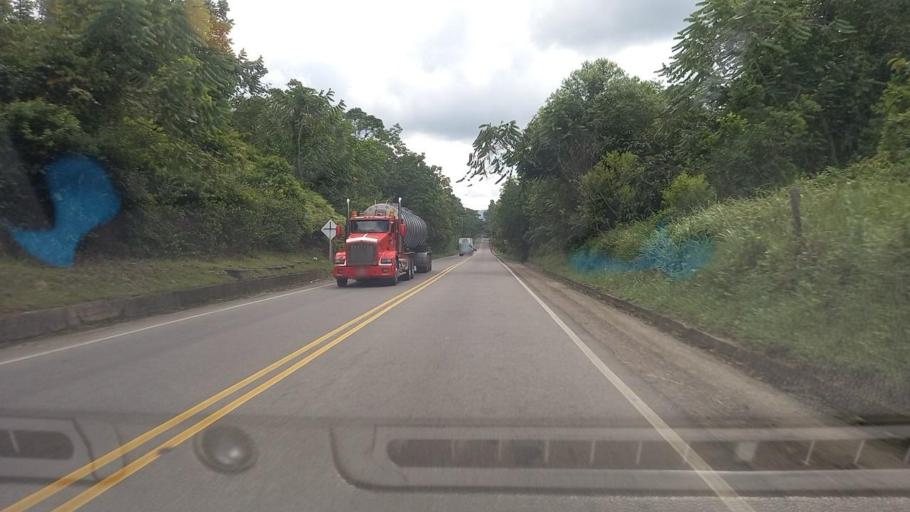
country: CO
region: Santander
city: Barrancabermeja
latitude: 7.1204
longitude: -73.6066
